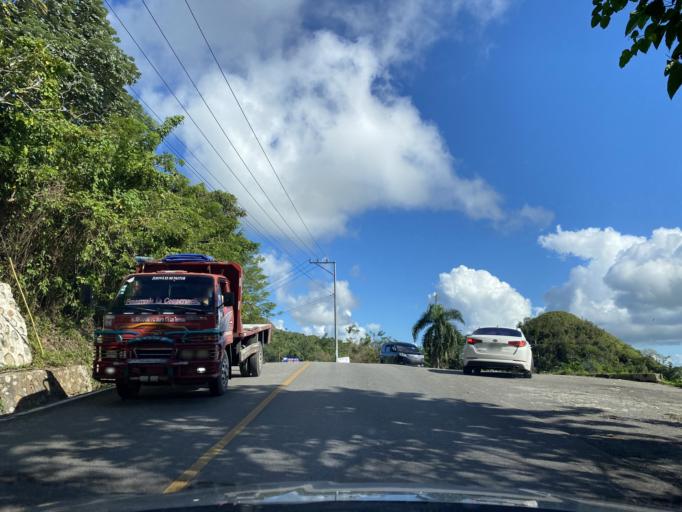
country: DO
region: Samana
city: Sanchez
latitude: 19.2418
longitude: -69.5959
